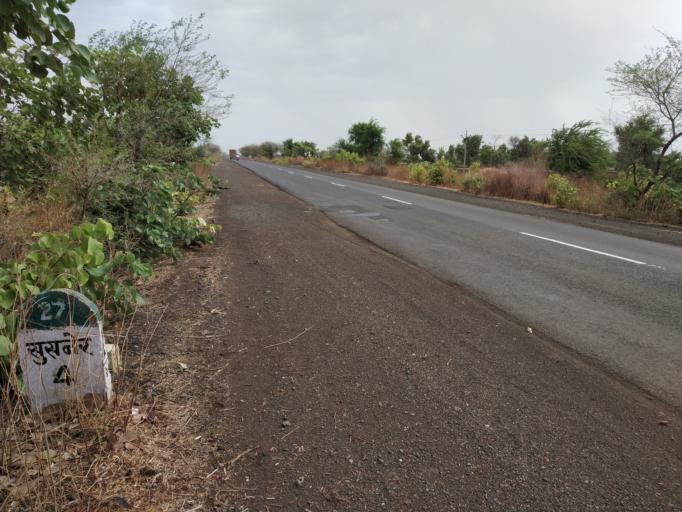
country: IN
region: Madhya Pradesh
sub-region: Shajapur
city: Susner
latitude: 23.9037
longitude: 76.1054
